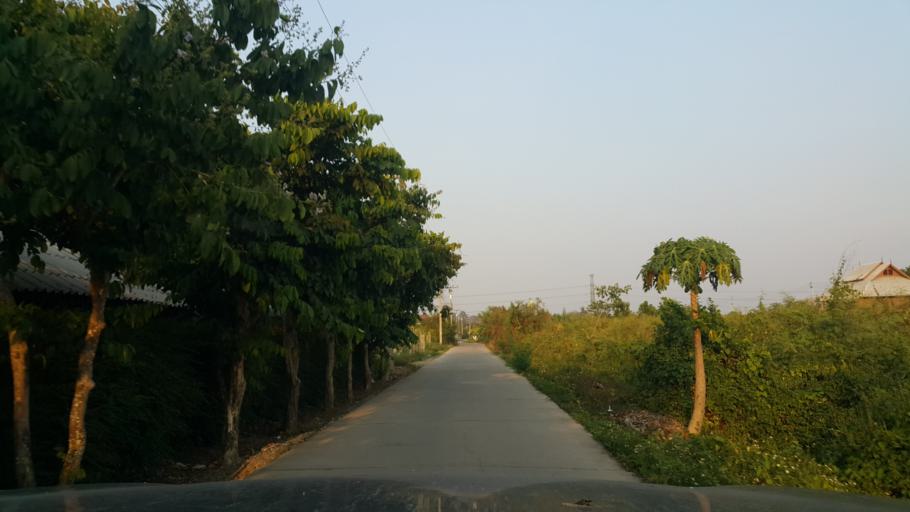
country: TH
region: Chiang Mai
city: Saraphi
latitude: 18.7209
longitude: 99.0128
